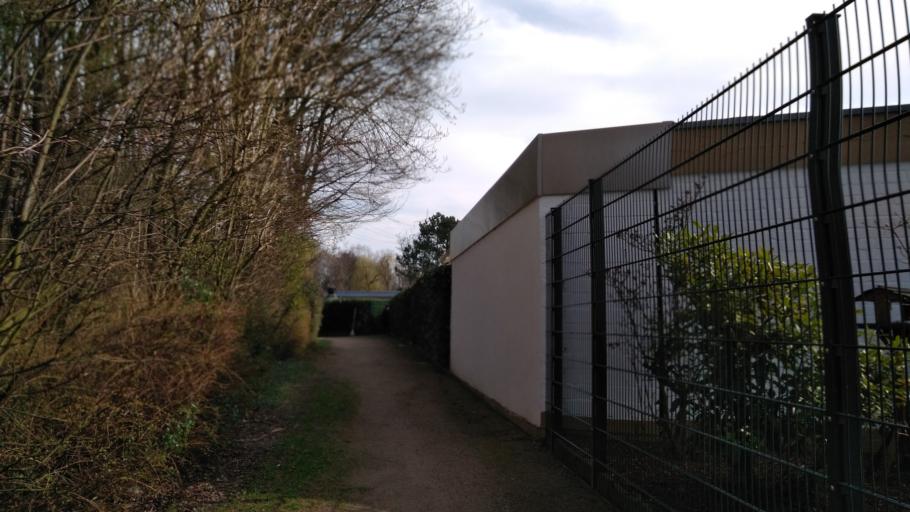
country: DE
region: North Rhine-Westphalia
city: Herten
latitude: 51.6082
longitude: 7.0974
